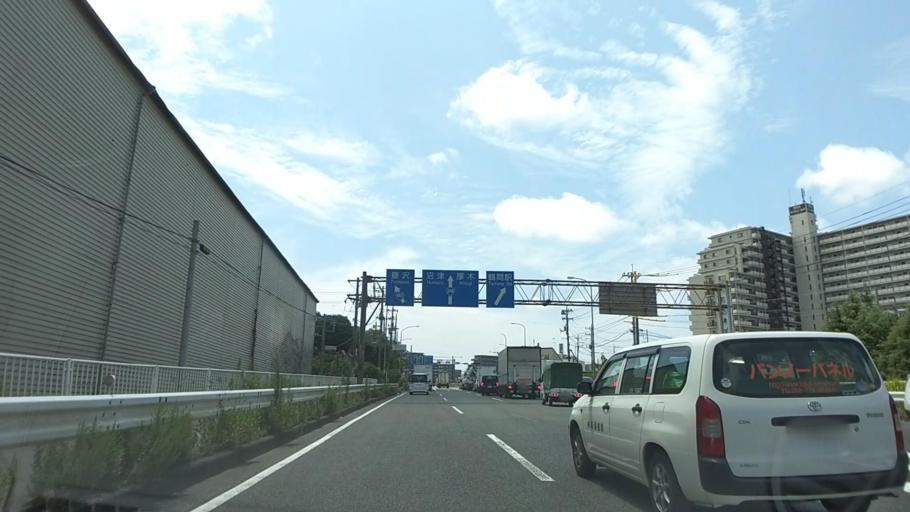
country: JP
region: Kanagawa
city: Minami-rinkan
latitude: 35.4949
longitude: 139.4651
